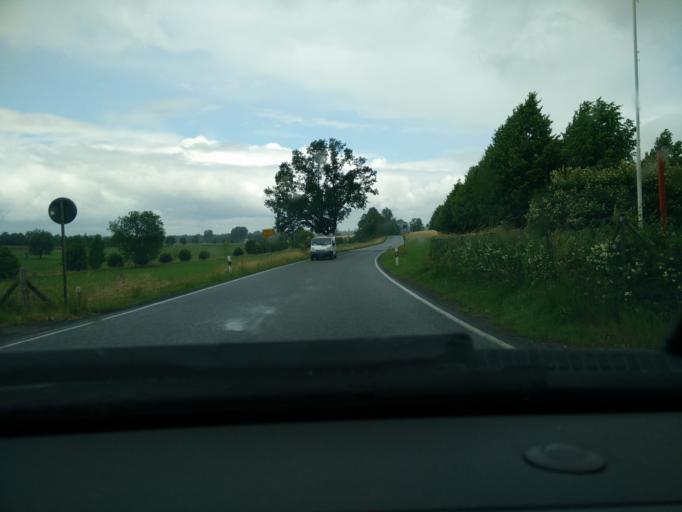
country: DE
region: Saxony
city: Grossbardau
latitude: 51.2074
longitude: 12.7032
